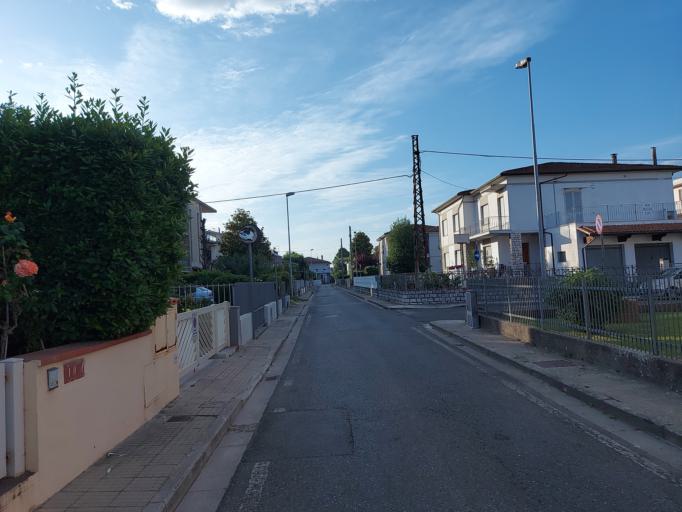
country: IT
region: Tuscany
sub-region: Province of Pisa
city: Cascina
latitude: 43.6884
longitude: 10.4952
